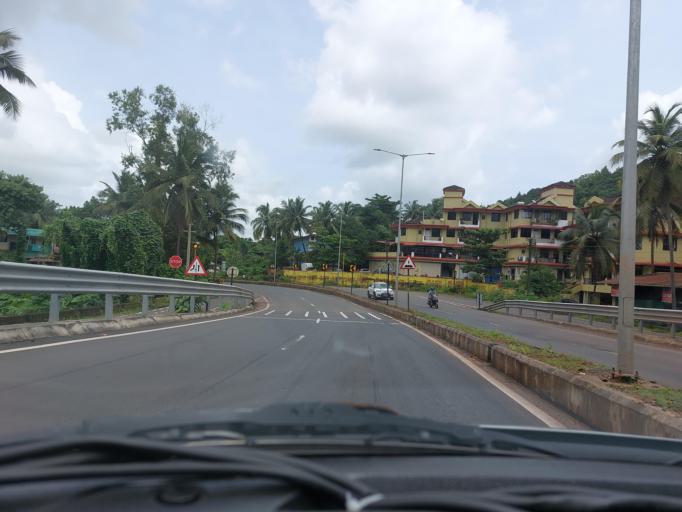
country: IN
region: Goa
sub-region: North Goa
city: Queula
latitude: 15.3862
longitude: 73.9999
